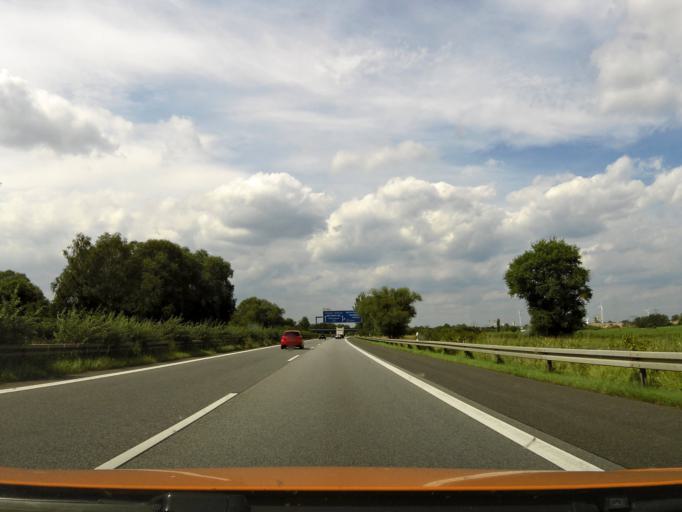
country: DE
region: Berlin
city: Buchholz
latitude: 52.6406
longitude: 13.4311
